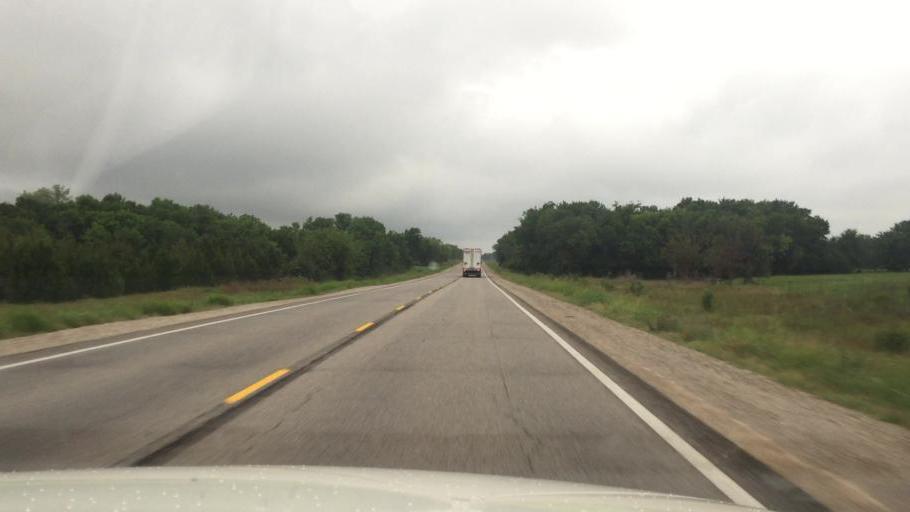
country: US
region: Kansas
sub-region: Montgomery County
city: Coffeyville
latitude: 37.1344
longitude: -95.5778
